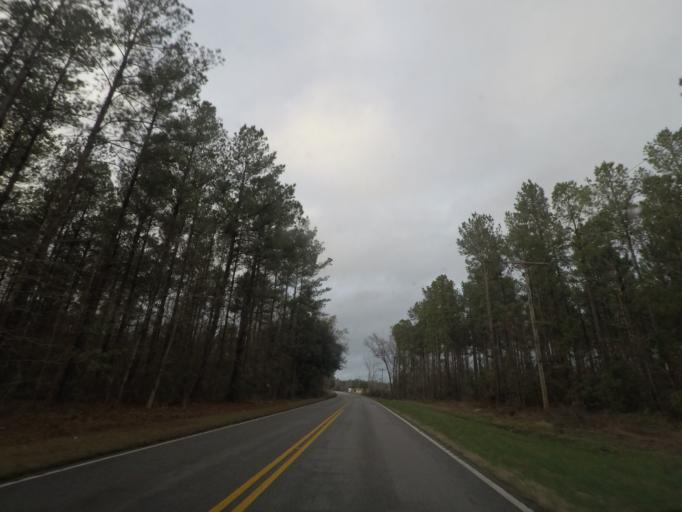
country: US
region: South Carolina
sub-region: Dorchester County
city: Saint George
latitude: 33.0701
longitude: -80.6336
